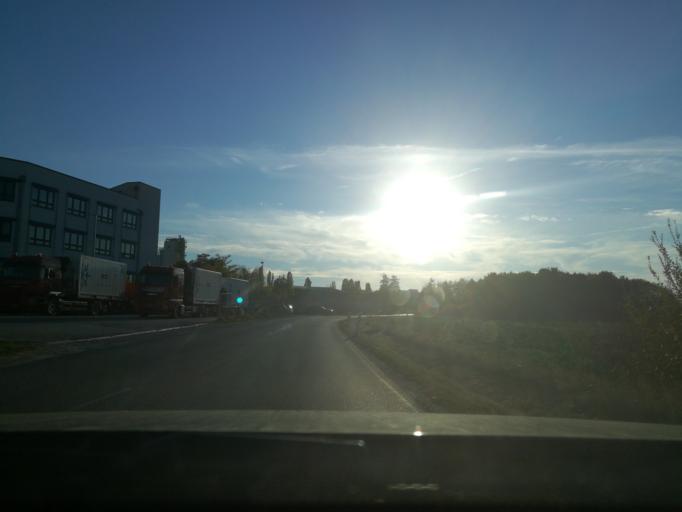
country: DE
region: Bavaria
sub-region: Regierungsbezirk Mittelfranken
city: Furth
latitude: 49.5232
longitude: 11.0051
